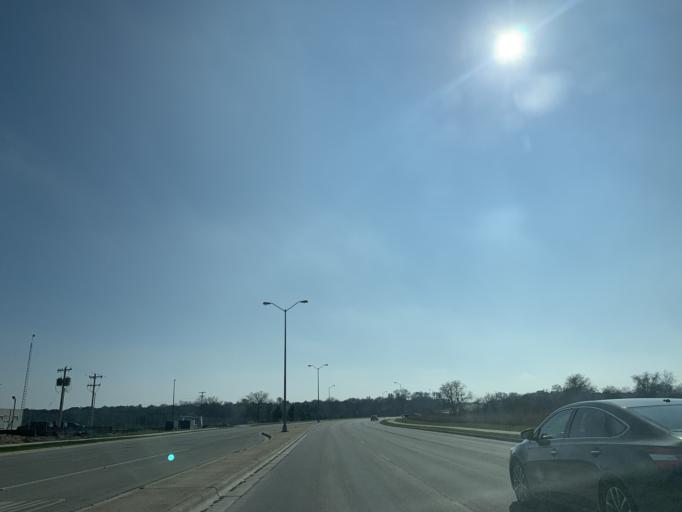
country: US
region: Texas
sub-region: Williamson County
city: Round Rock
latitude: 30.5173
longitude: -97.6375
